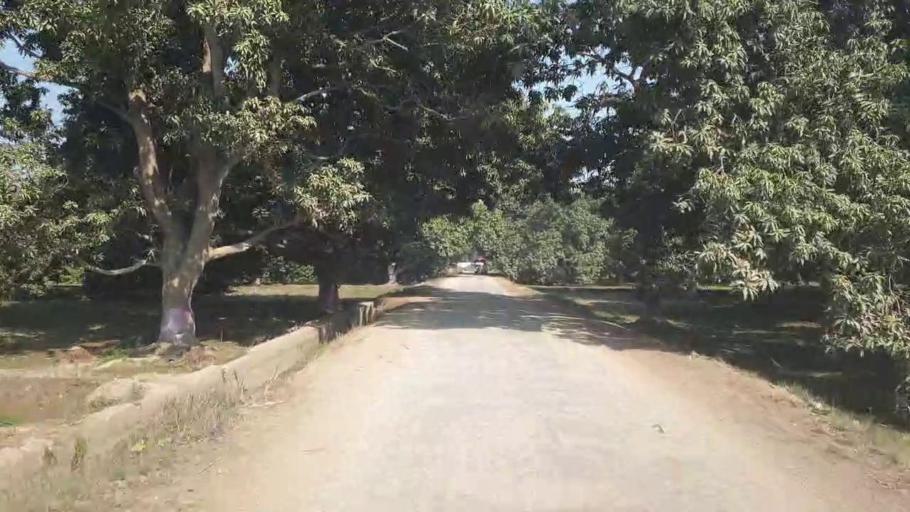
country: PK
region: Sindh
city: Tando Allahyar
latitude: 25.4785
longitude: 68.7840
